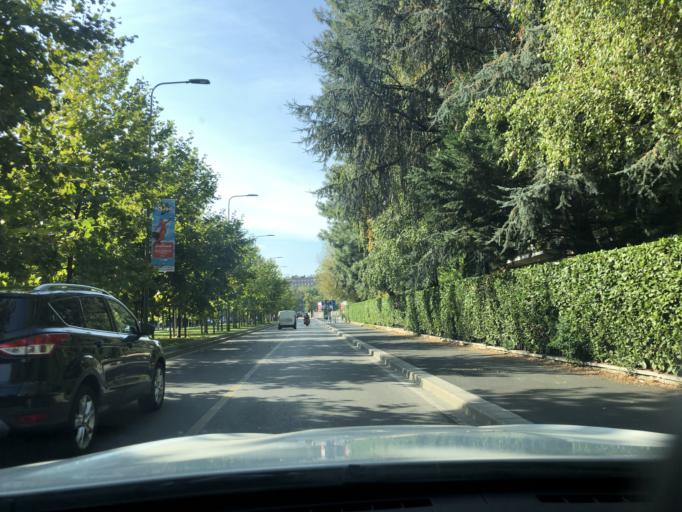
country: IT
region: Lombardy
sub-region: Citta metropolitana di Milano
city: Cesano Boscone
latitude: 45.4763
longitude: 9.1164
